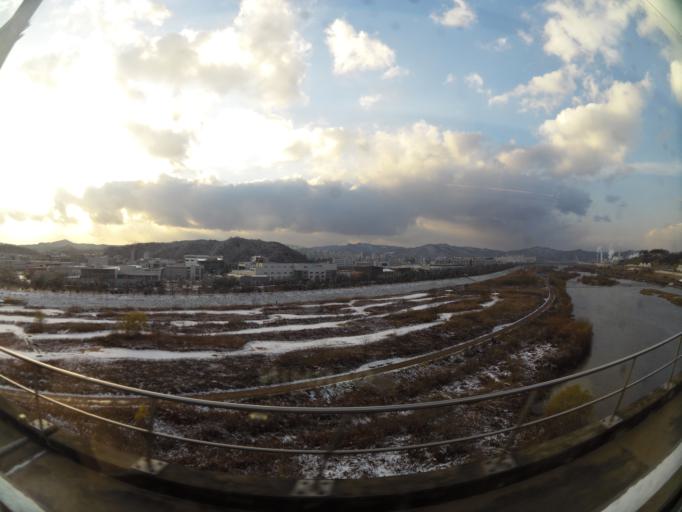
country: KR
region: Daejeon
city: Songgang-dong
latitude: 36.4196
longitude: 127.4158
